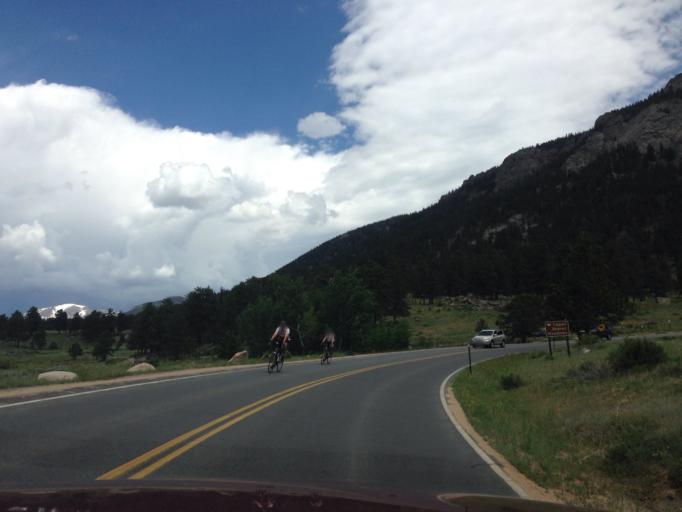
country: US
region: Colorado
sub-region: Larimer County
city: Estes Park
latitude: 40.3688
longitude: -105.5925
